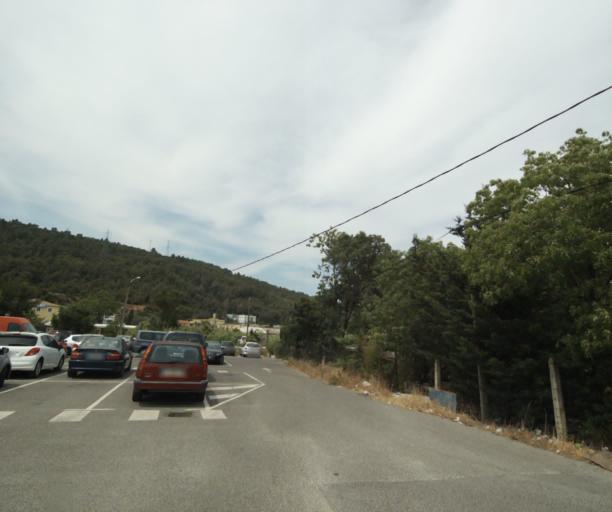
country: FR
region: Provence-Alpes-Cote d'Azur
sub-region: Departement du Var
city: La Garde
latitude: 43.1432
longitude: 6.0254
